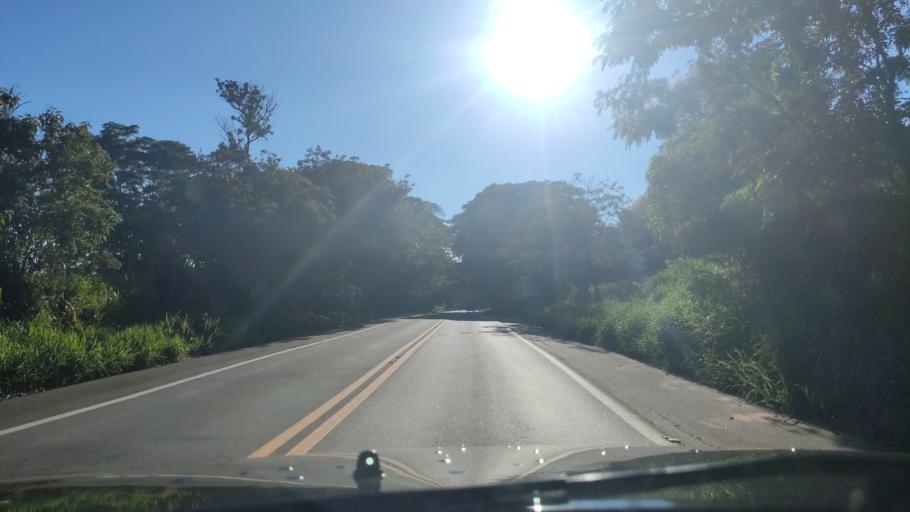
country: BR
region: Sao Paulo
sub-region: Socorro
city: Socorro
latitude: -22.5598
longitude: -46.5588
